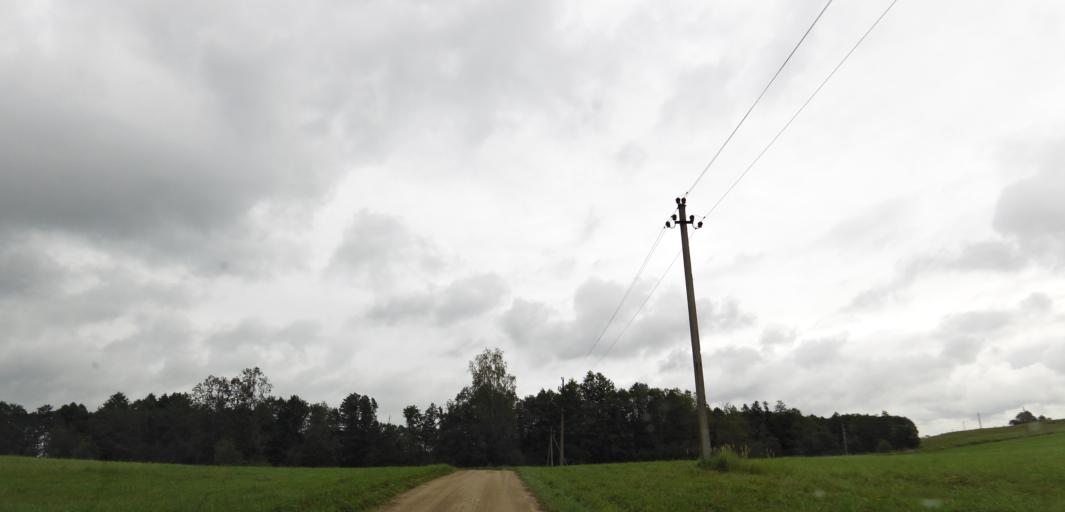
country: LT
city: Moletai
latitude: 55.3356
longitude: 25.3769
